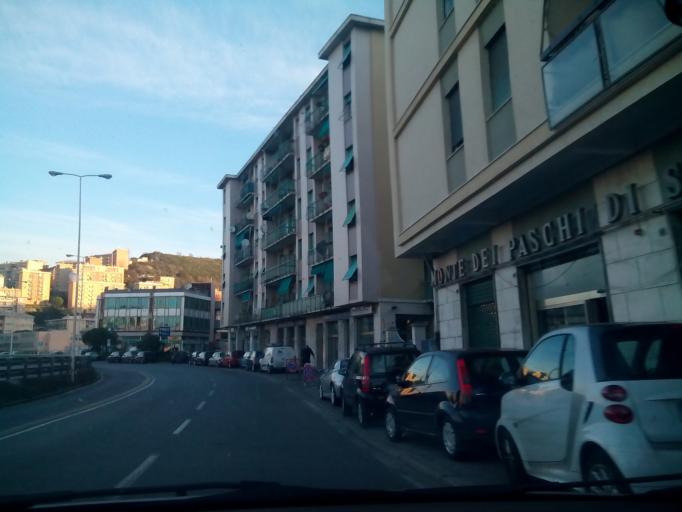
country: IT
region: Liguria
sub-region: Provincia di Genova
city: Genoa
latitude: 44.3995
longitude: 8.9893
